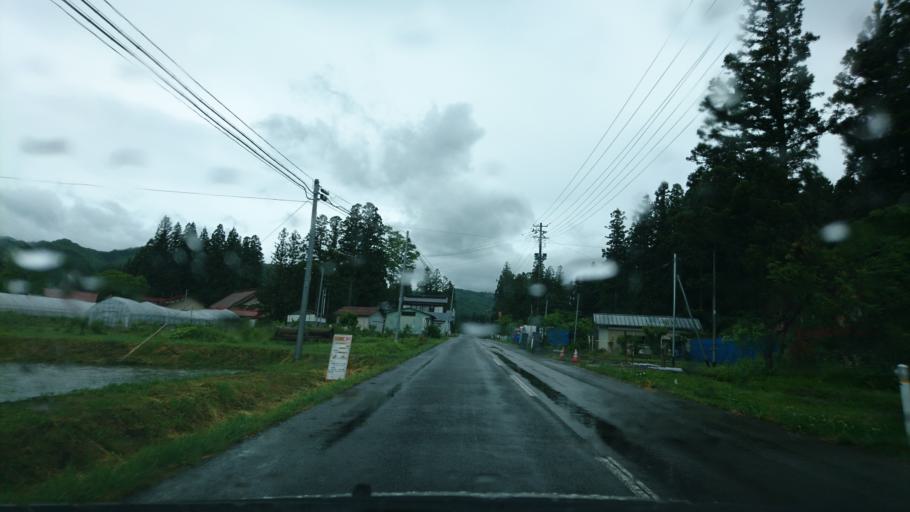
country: JP
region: Iwate
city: Ichinoseki
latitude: 38.9822
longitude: 140.9163
